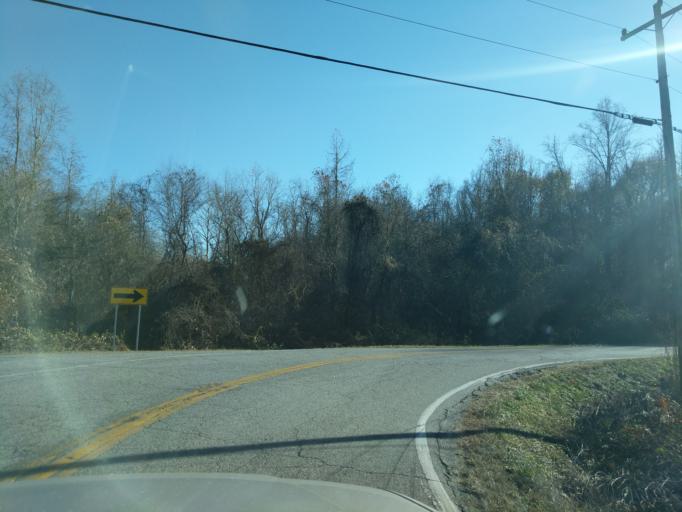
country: US
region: South Carolina
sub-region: Spartanburg County
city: Landrum
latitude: 35.1198
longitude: -82.1450
